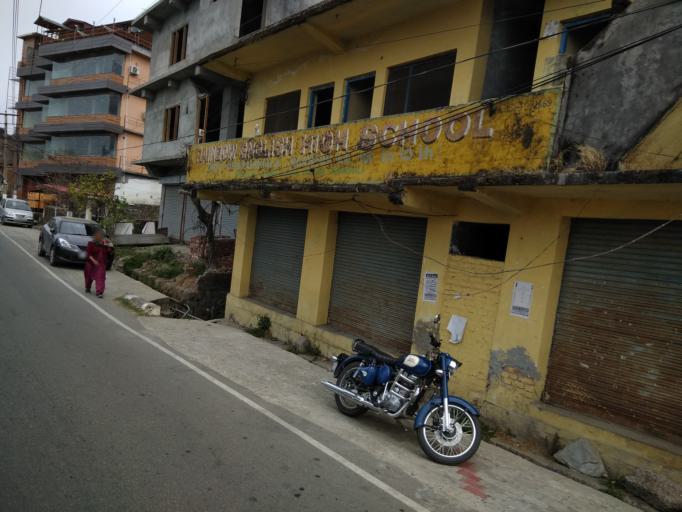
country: IN
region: Himachal Pradesh
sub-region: Kangra
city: Dharmsala
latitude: 32.2033
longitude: 76.3313
